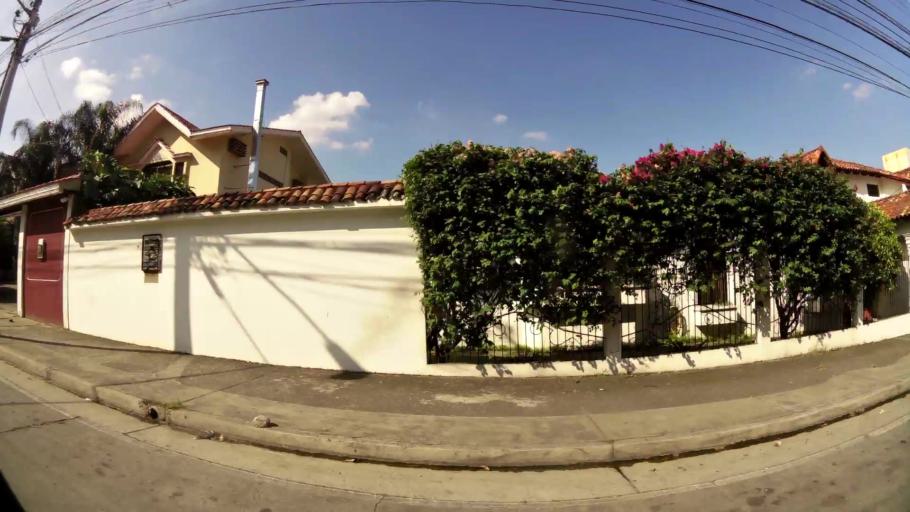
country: EC
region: Guayas
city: Guayaquil
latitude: -2.1695
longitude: -79.9439
